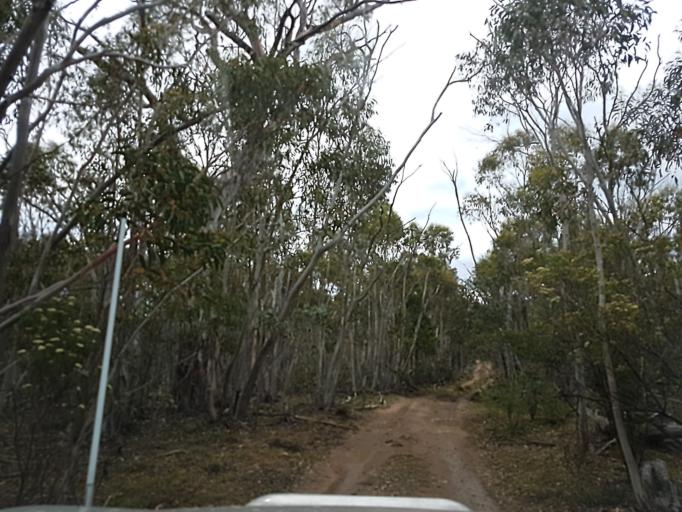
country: AU
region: New South Wales
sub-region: Snowy River
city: Jindabyne
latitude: -36.8599
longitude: 148.2645
